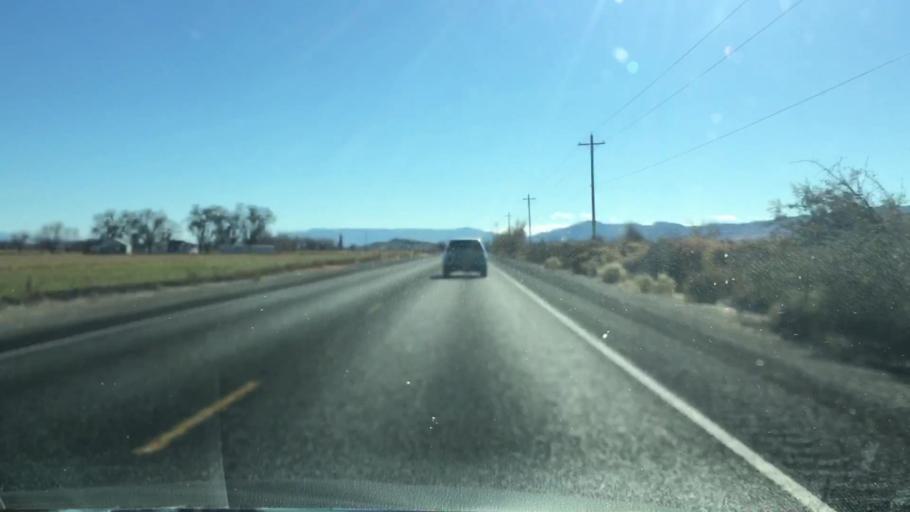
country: US
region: Nevada
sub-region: Lyon County
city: Yerington
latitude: 39.0654
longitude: -119.1813
